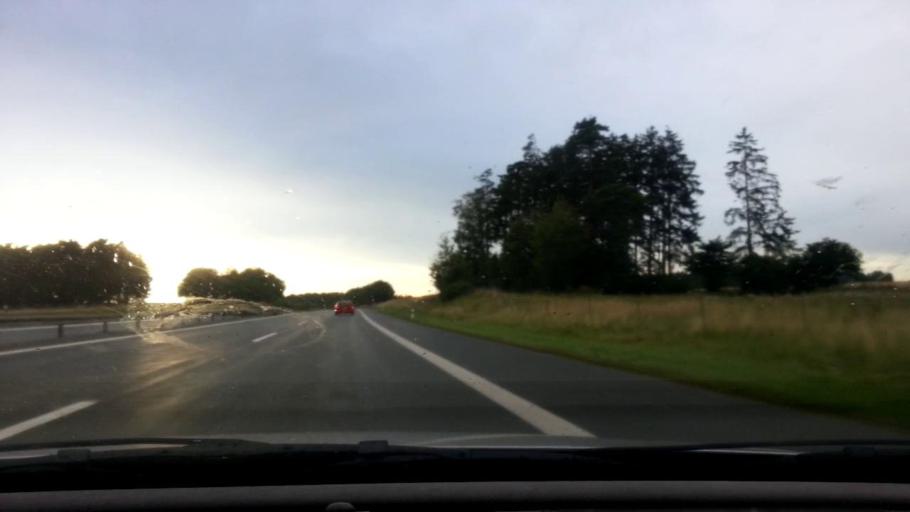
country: DE
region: Bavaria
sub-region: Upper Franconia
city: Stadelhofen
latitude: 50.0075
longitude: 11.2504
